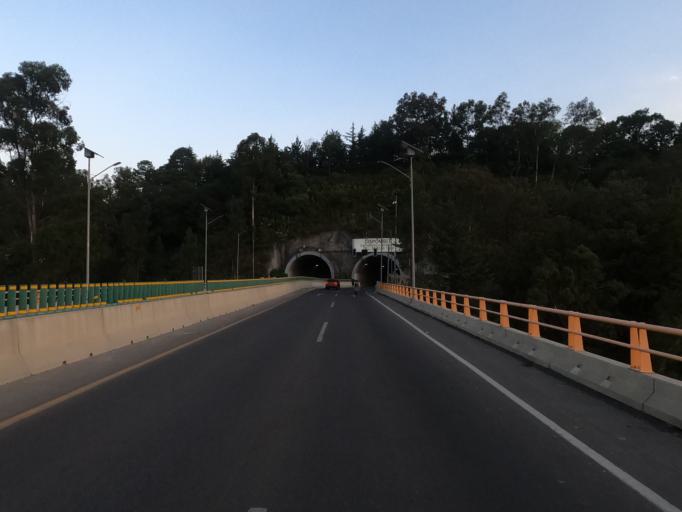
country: MX
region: Mexico
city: San Bartolome Coatepec
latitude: 19.4126
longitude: -99.2843
